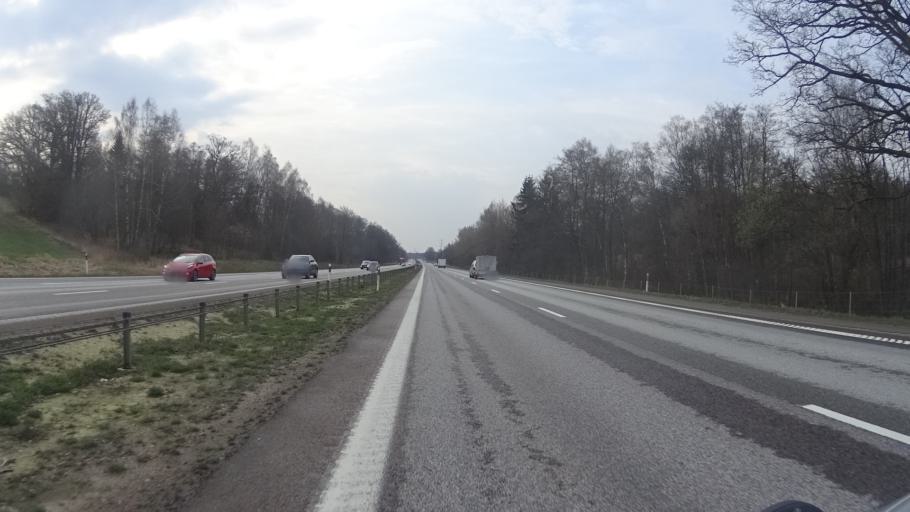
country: SE
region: Halland
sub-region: Halmstads Kommun
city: Halmstad
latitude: 56.7073
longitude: 12.8897
